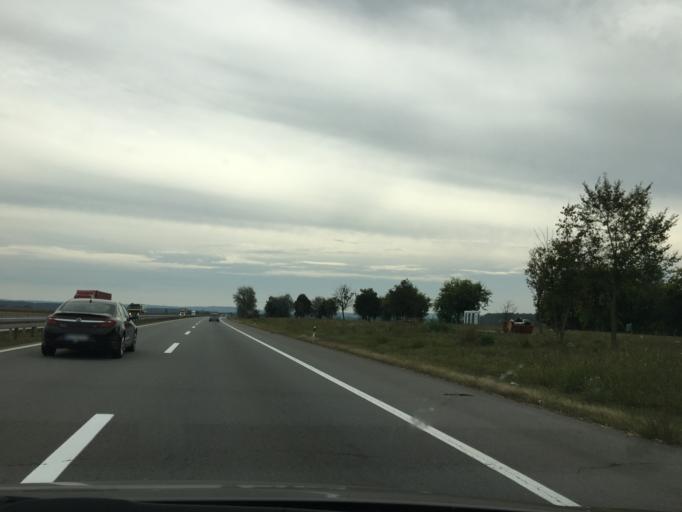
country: RS
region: Autonomna Pokrajina Vojvodina
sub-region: Juznobacki Okrug
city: Kovilj
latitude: 45.2177
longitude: 20.0627
